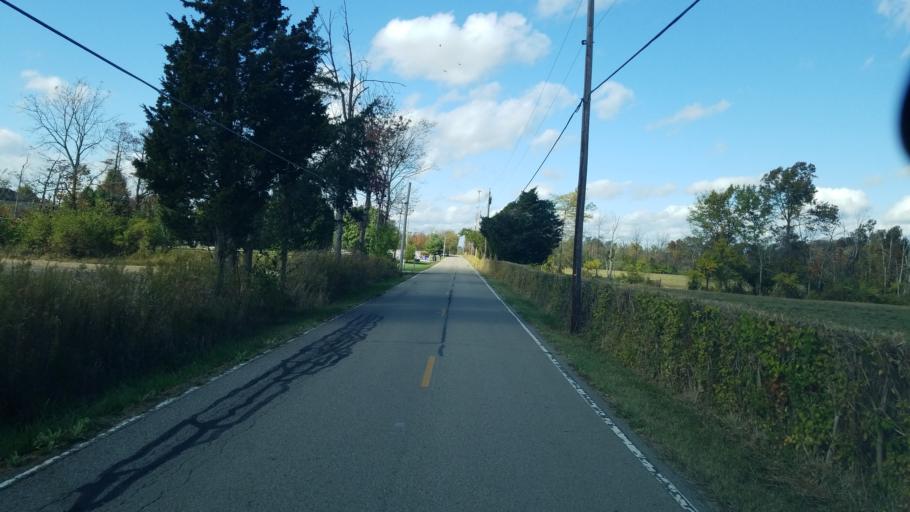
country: US
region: Ohio
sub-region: Warren County
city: Lebanon
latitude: 39.4015
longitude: -84.1651
